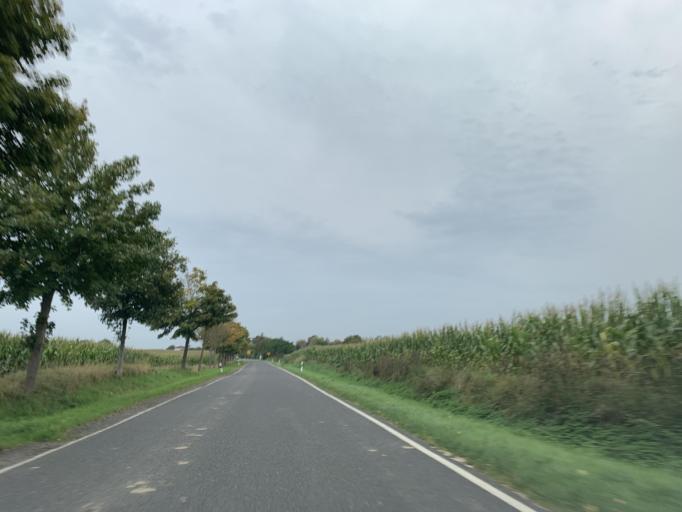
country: DE
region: Mecklenburg-Vorpommern
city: Woldegk
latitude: 53.3297
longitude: 13.5352
